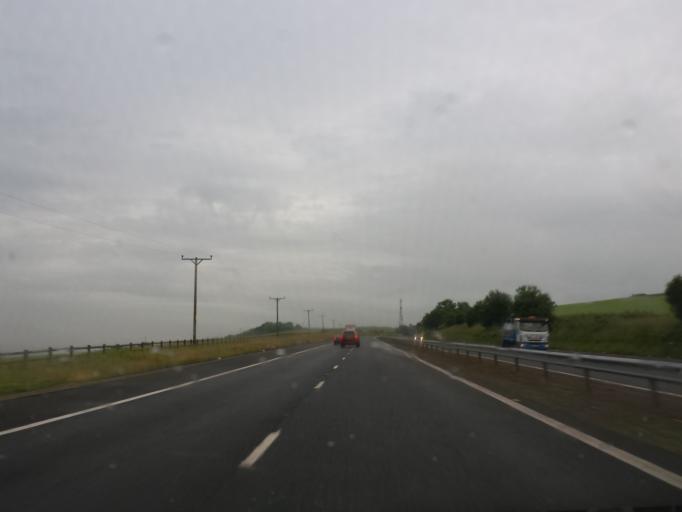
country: GB
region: Scotland
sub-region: Perth and Kinross
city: Perth
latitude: 56.3792
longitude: -3.4546
